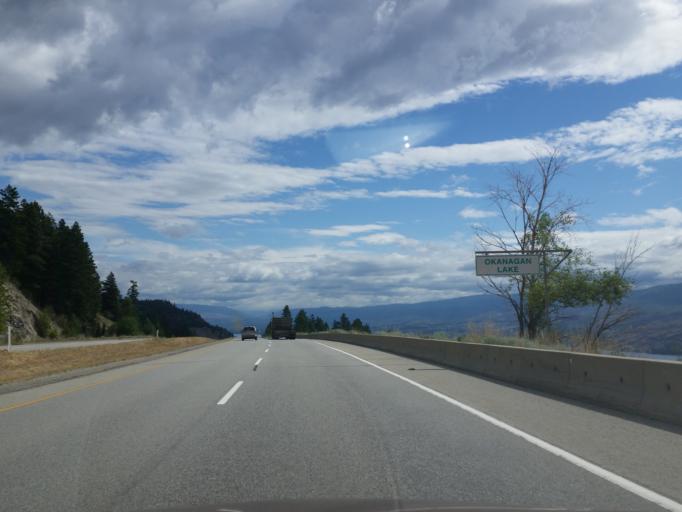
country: CA
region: British Columbia
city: Peachland
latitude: 49.8001
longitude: -119.6926
